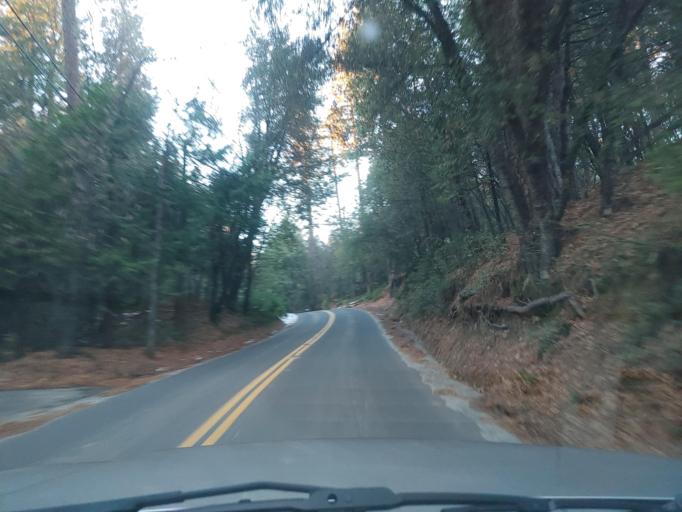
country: US
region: California
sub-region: Tuolumne County
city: Twain Harte
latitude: 38.0294
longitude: -120.2519
